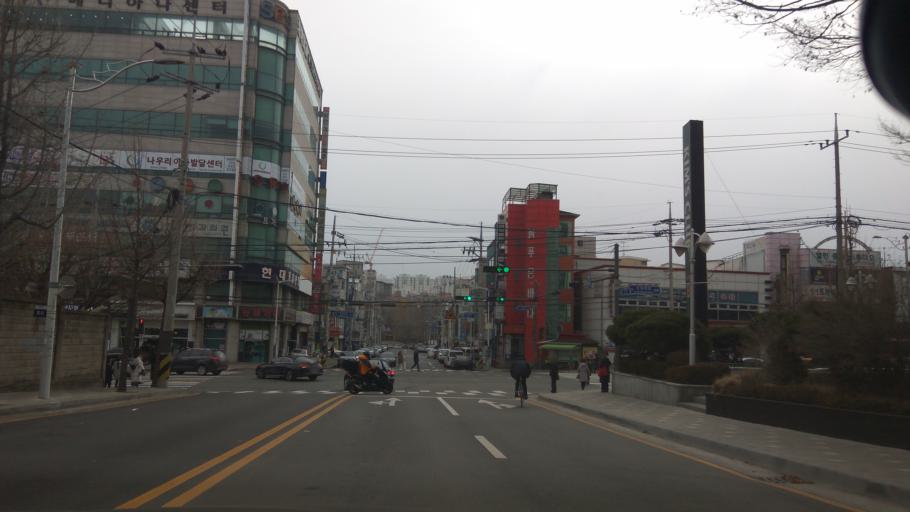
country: KR
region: Incheon
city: Incheon
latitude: 37.4909
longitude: 126.7111
